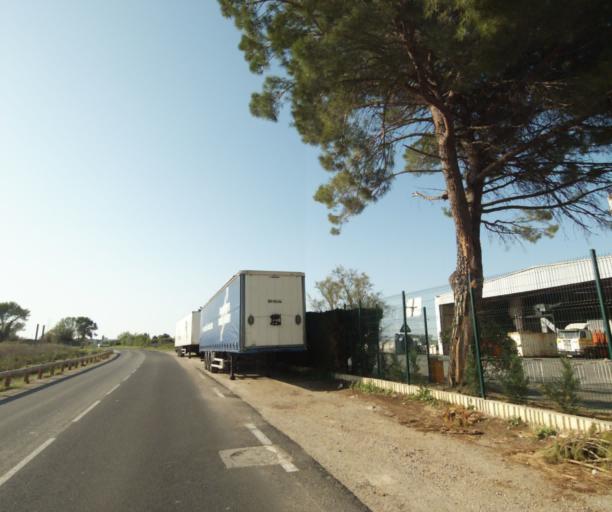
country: FR
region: Languedoc-Roussillon
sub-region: Departement de l'Herault
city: Laverune
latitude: 43.5930
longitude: 3.7984
